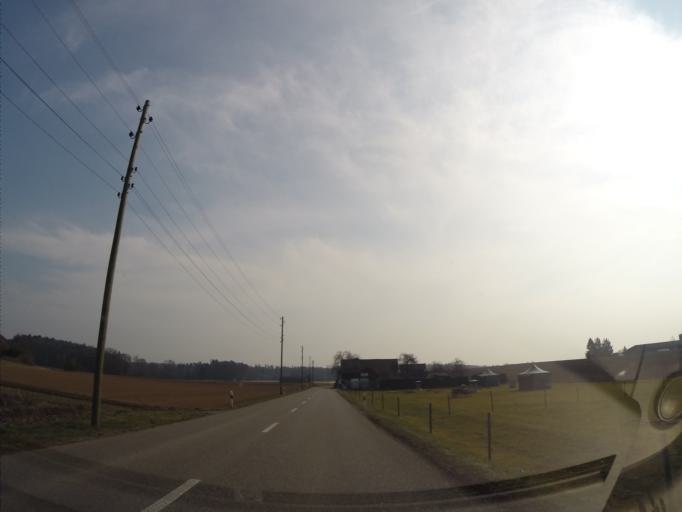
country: CH
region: Zurich
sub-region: Bezirk Andelfingen
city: Kleinandelfingen
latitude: 47.6314
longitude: 8.6921
